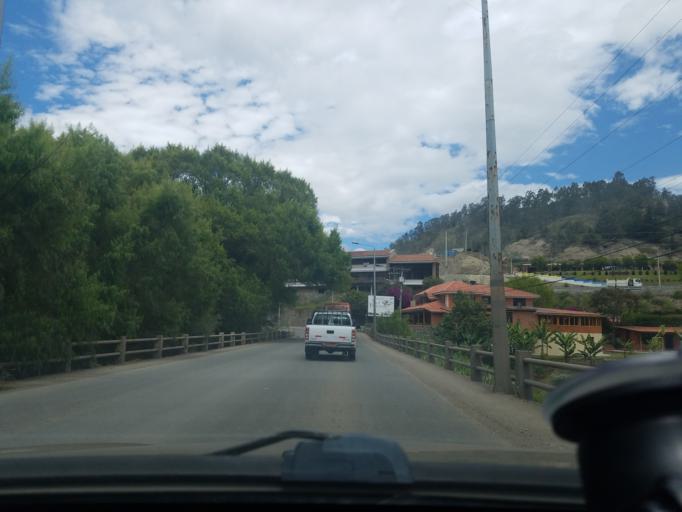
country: EC
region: Azuay
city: Llacao
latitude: -2.8348
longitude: -78.8763
